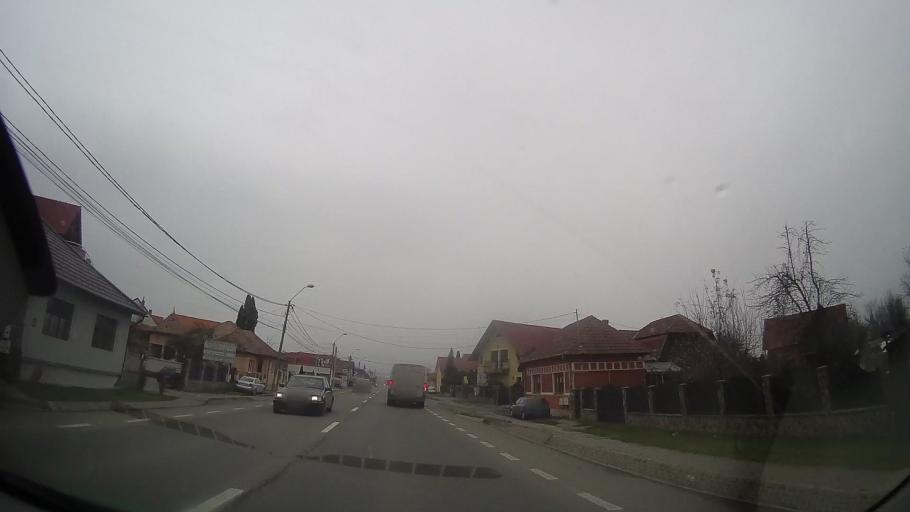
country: RO
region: Mures
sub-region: Comuna Santana de Mures
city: Santana de Mures
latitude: 46.5869
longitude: 24.5374
